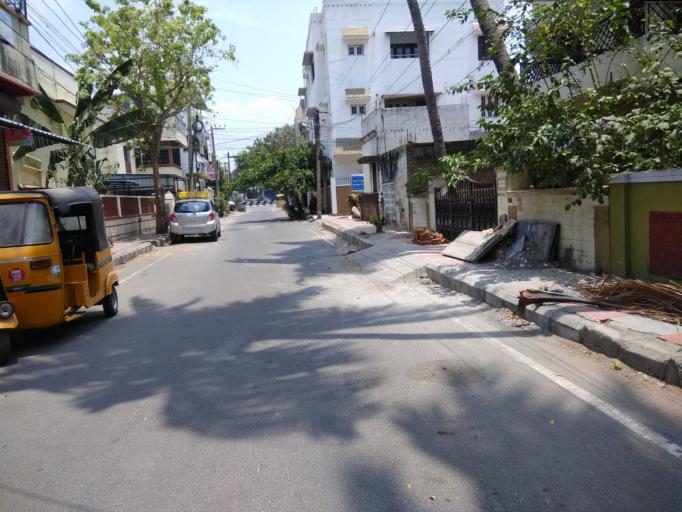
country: IN
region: Tamil Nadu
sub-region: Kancheepuram
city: Saint Thomas Mount
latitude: 12.9891
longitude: 80.1988
